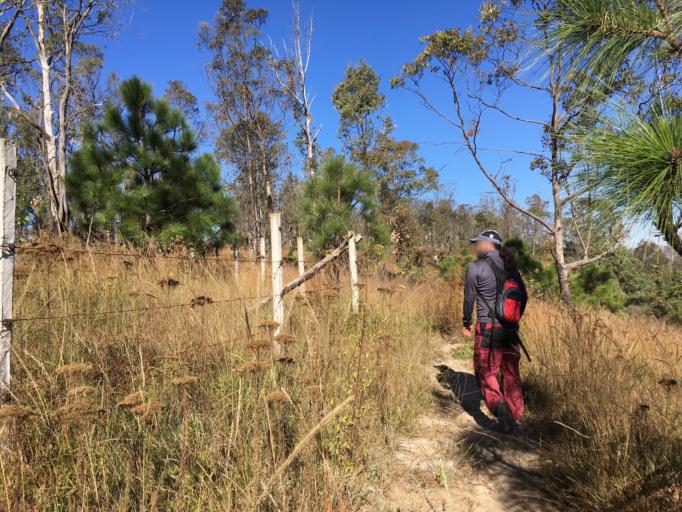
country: MX
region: Michoacan
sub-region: Morelia
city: Montana Monarca (Punta Altozano)
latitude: 19.6661
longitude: -101.1459
